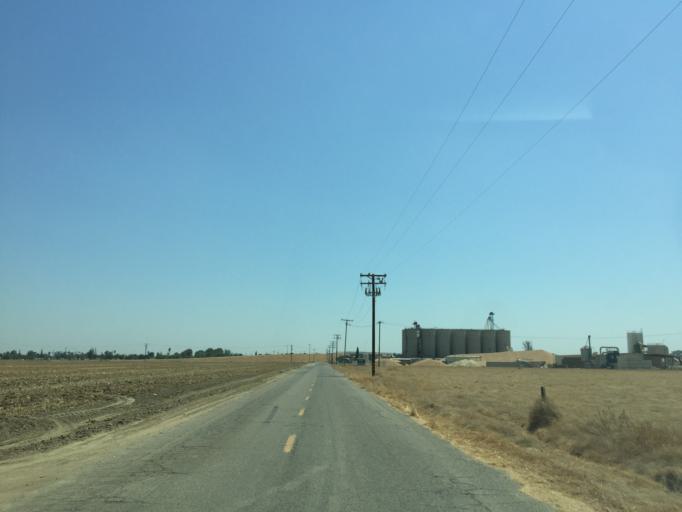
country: US
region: California
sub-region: Tulare County
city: Goshen
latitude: 36.3599
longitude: -119.4214
